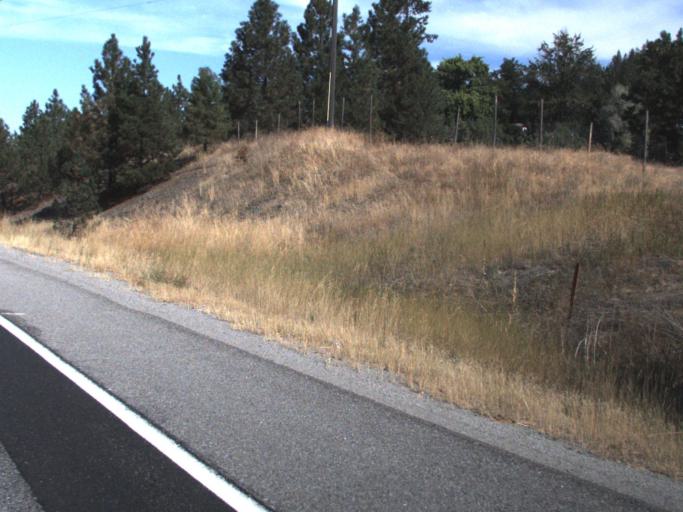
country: US
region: Washington
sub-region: Stevens County
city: Chewelah
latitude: 48.1895
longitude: -117.7006
